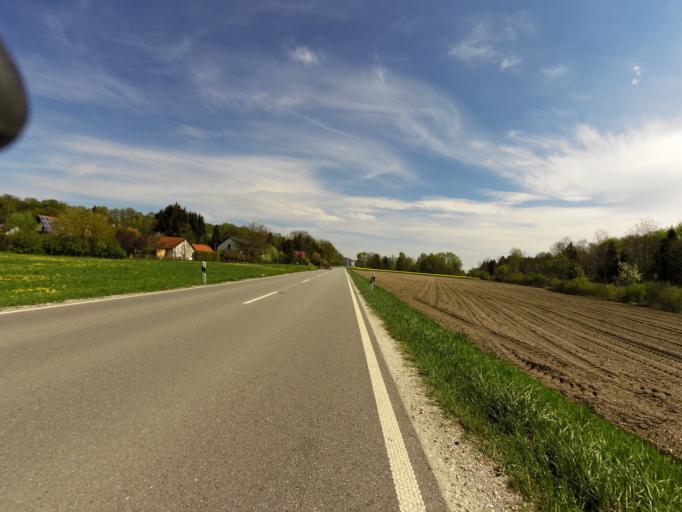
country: DE
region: Bavaria
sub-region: Upper Bavaria
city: Wang
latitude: 48.5082
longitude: 11.9699
